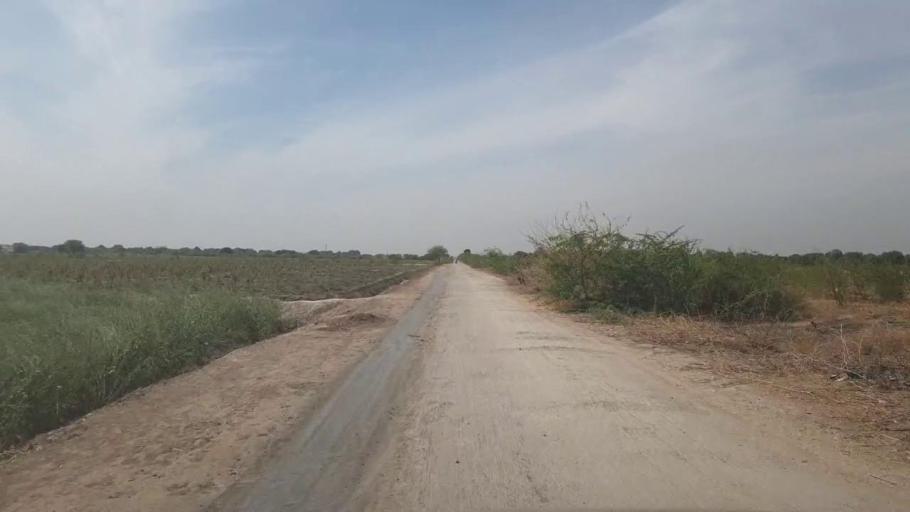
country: PK
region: Sindh
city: Kunri
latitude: 25.2120
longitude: 69.6105
